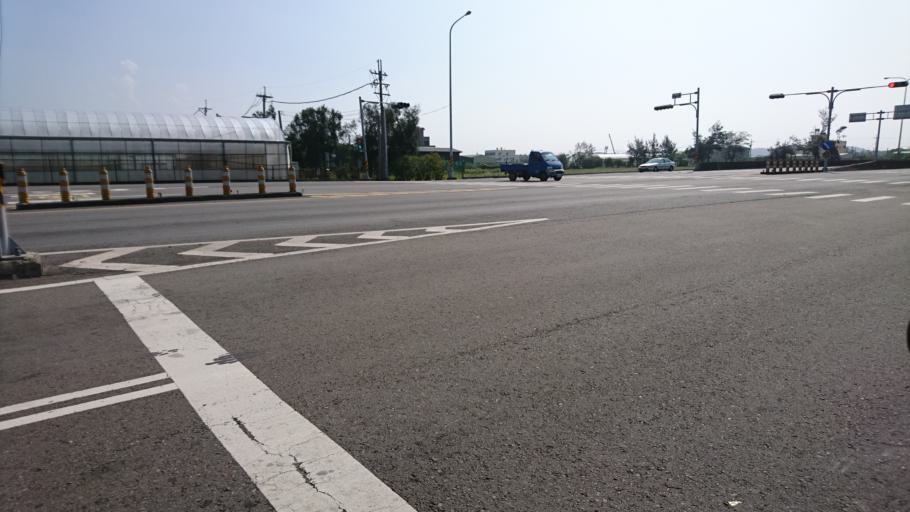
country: TW
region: Taiwan
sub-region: Miaoli
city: Miaoli
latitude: 24.6856
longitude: 120.8517
